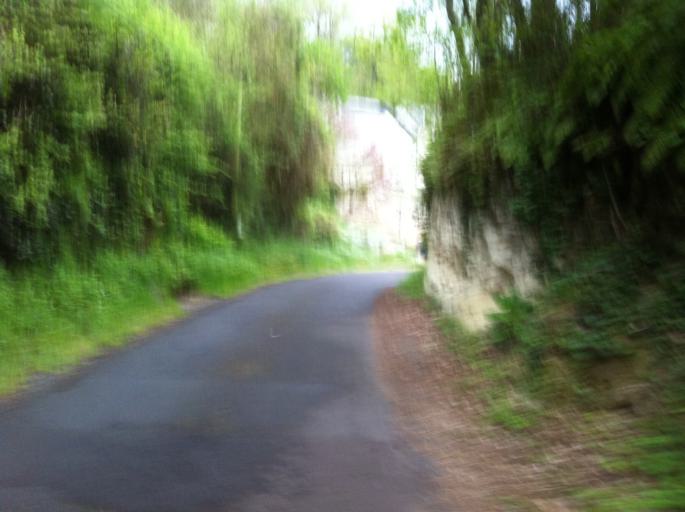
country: FR
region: Pays de la Loire
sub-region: Departement de Maine-et-Loire
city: Saint-Martin-de-la-Place
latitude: 47.2958
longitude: -0.1417
